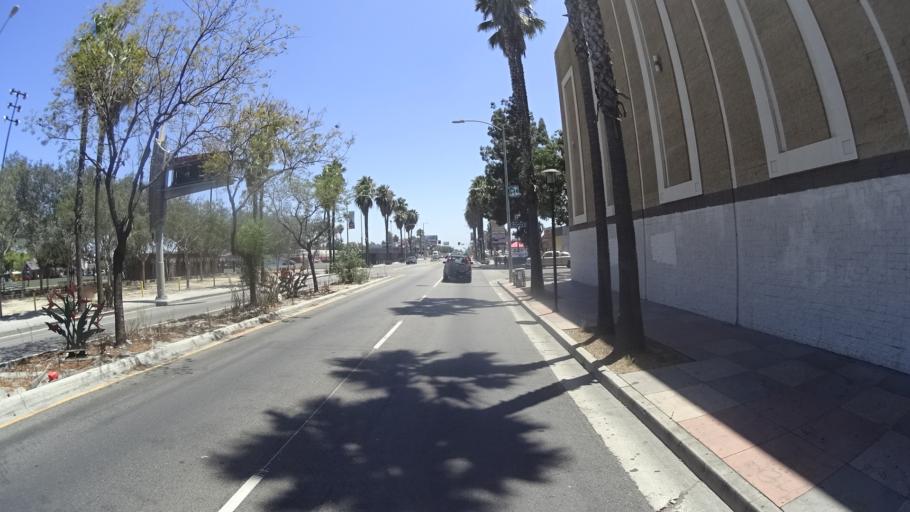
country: US
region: California
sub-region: Los Angeles County
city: View Park-Windsor Hills
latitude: 34.0125
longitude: -118.2916
